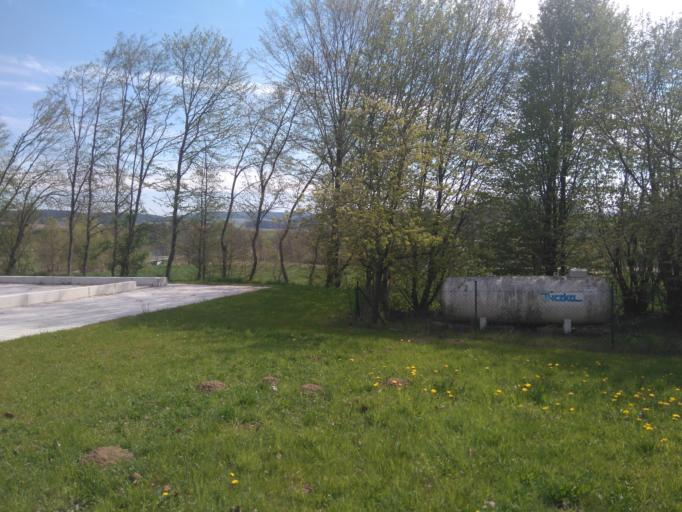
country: DE
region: Bavaria
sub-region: Upper Palatinate
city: Altendorf
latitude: 49.3996
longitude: 12.3067
